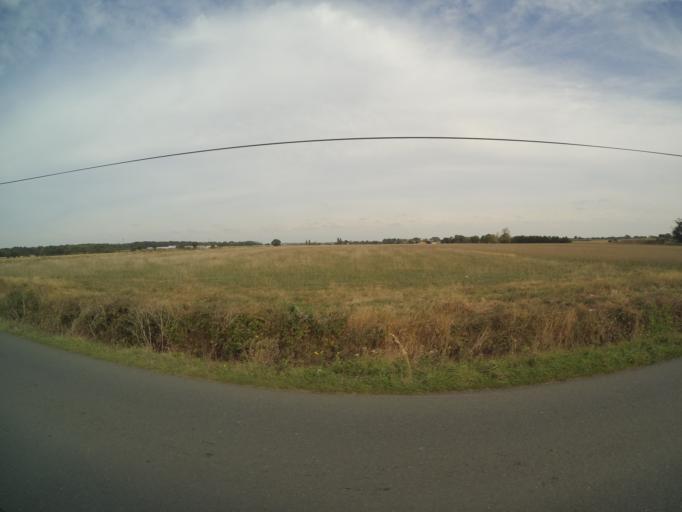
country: FR
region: Pays de la Loire
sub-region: Departement de Maine-et-Loire
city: Melay
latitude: 47.2102
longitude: -0.6874
